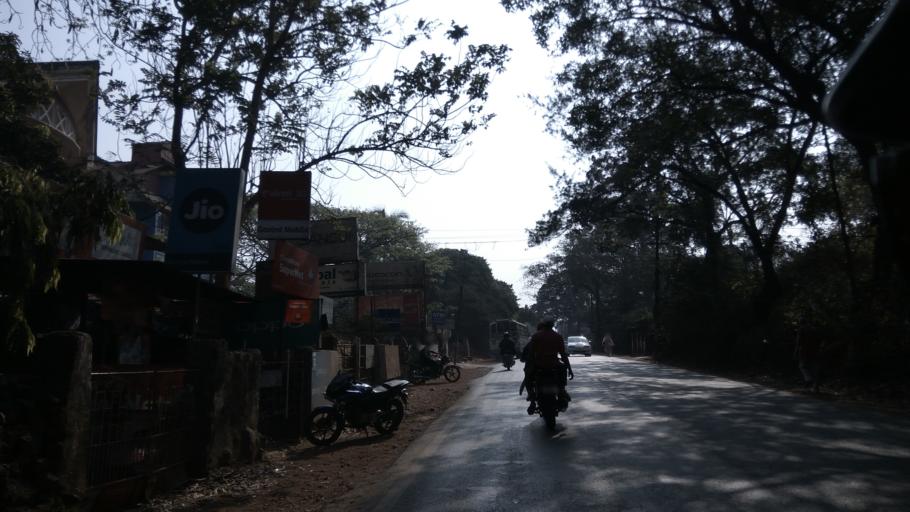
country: IN
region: Goa
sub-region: North Goa
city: Jua
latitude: 15.4961
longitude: 73.9335
